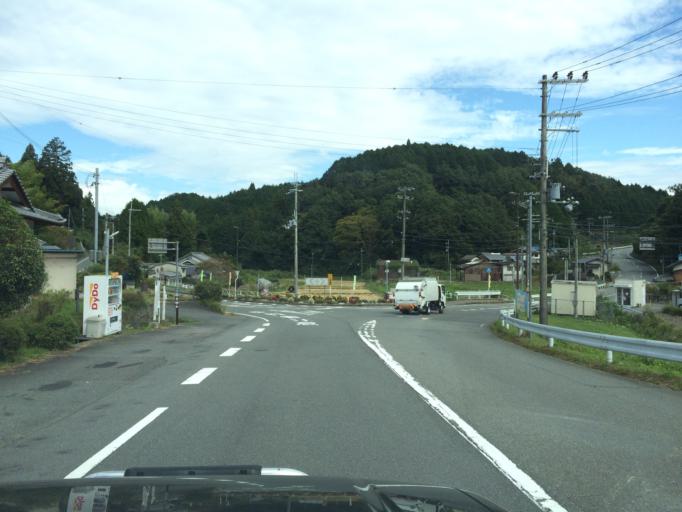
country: JP
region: Nara
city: Haibara-akanedai
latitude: 34.6740
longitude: 135.9500
